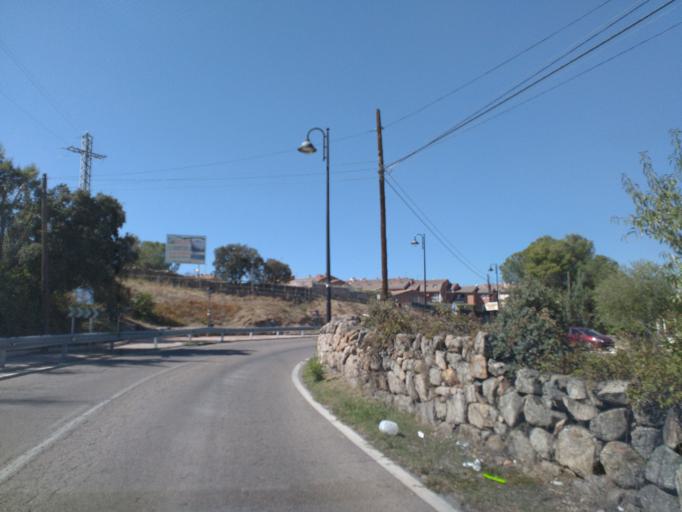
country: ES
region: Madrid
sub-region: Provincia de Madrid
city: Galapagar
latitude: 40.5764
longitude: -3.9977
